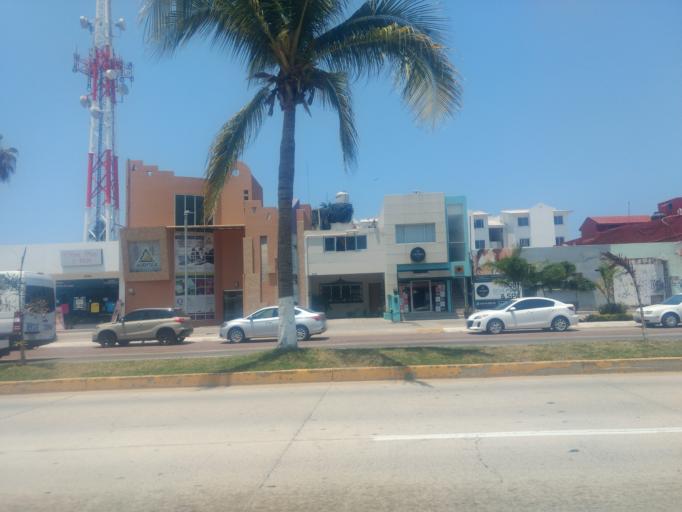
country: MX
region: Colima
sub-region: Manzanillo
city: Manzanillo
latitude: 19.0980
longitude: -104.3223
